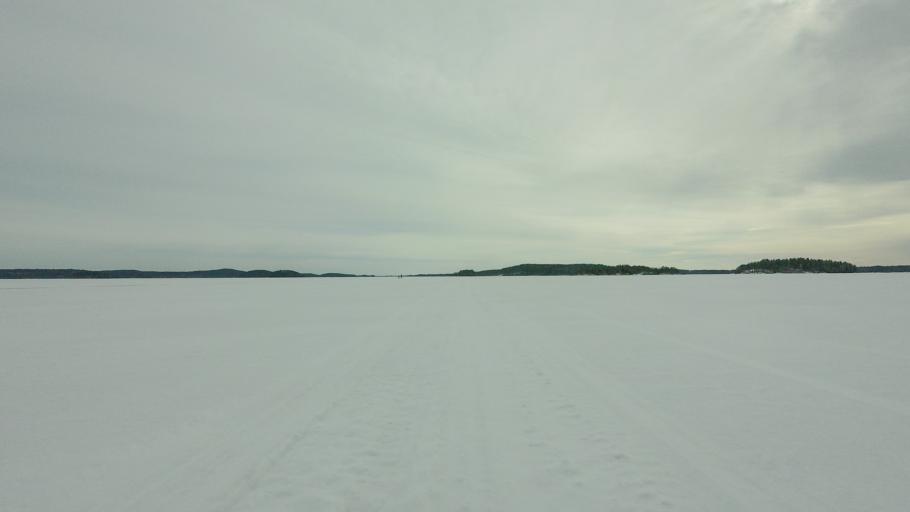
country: FI
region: Southern Savonia
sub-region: Savonlinna
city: Rantasalmi
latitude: 62.1034
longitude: 28.4294
